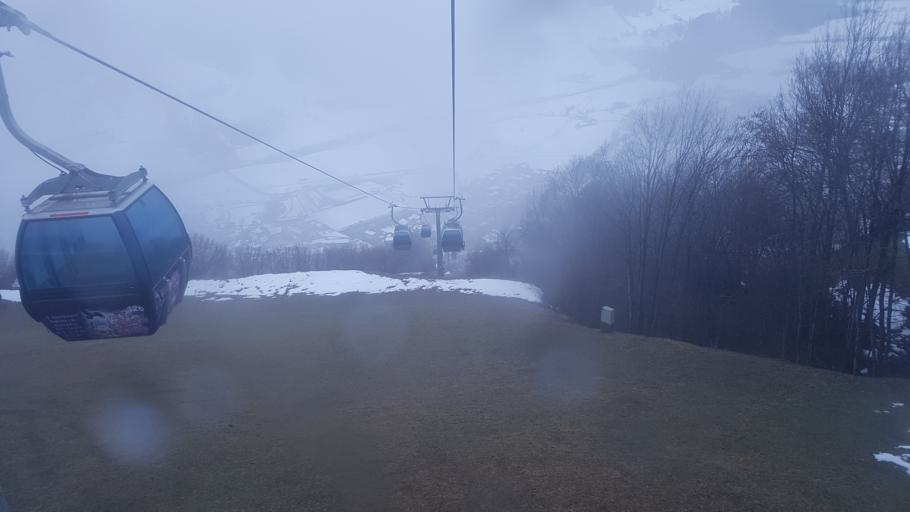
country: AT
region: Salzburg
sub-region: Politischer Bezirk Zell am See
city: Neukirchen am Grossvenediger
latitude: 47.2600
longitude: 12.2809
